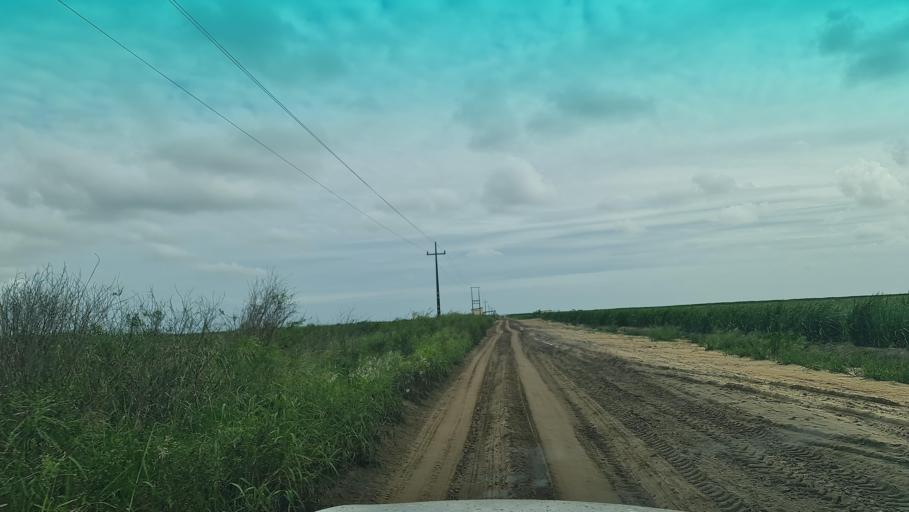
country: MZ
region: Maputo
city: Manhica
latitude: -25.4519
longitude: 32.8391
